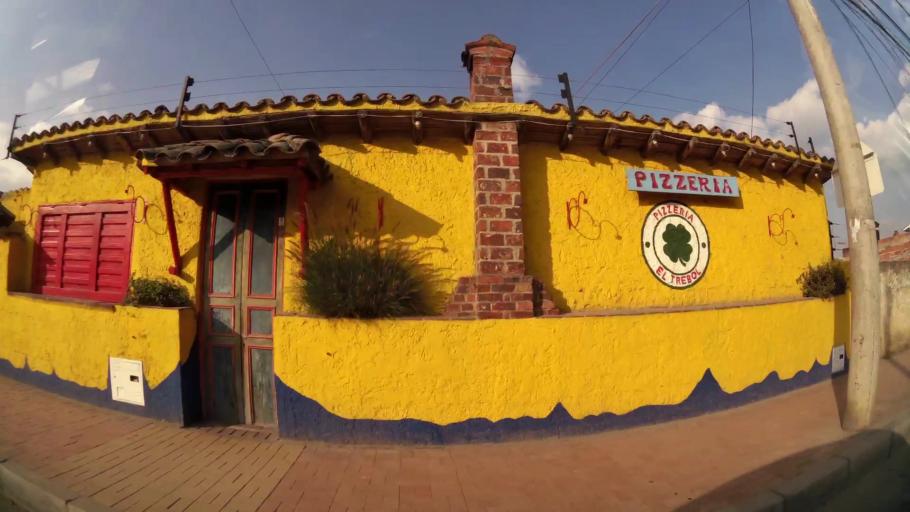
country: CO
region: Cundinamarca
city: Cota
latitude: 4.8140
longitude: -74.1029
